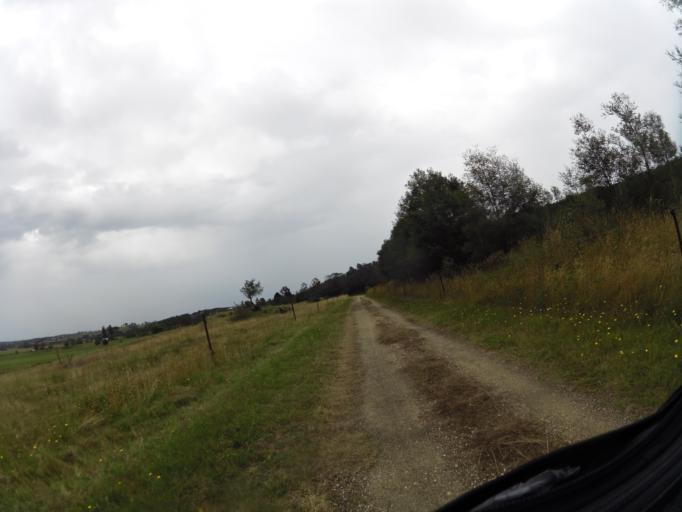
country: AU
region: Victoria
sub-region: East Gippsland
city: Lakes Entrance
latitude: -37.7061
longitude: 147.8199
